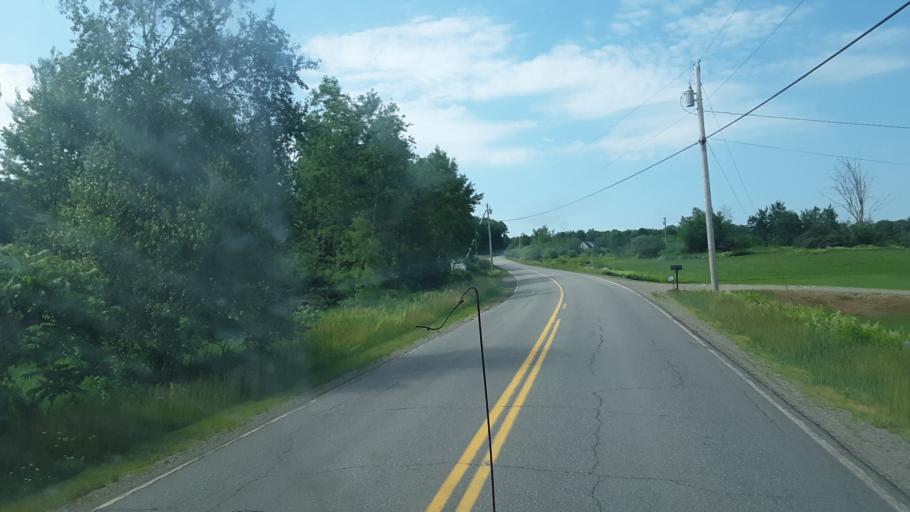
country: US
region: Maine
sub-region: Waldo County
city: Frankfort
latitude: 44.5932
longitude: -68.9435
